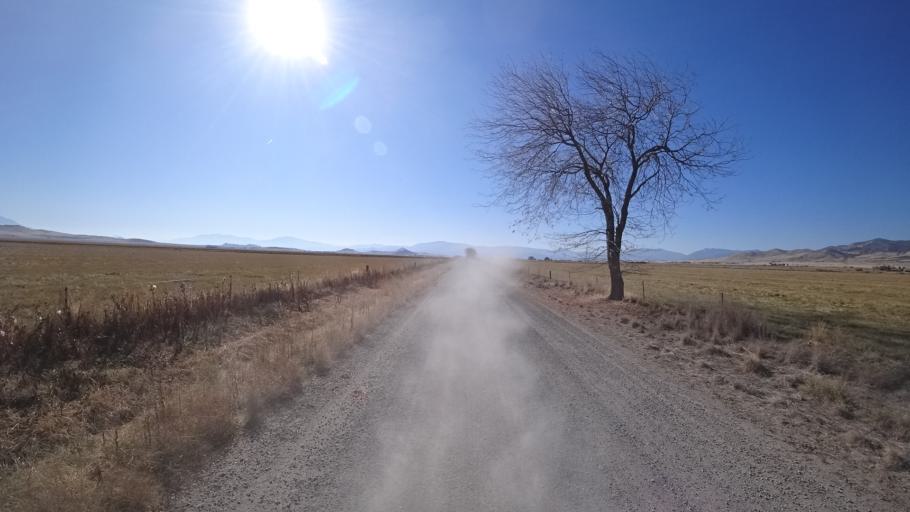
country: US
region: California
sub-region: Siskiyou County
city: Montague
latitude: 41.7927
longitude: -122.4570
